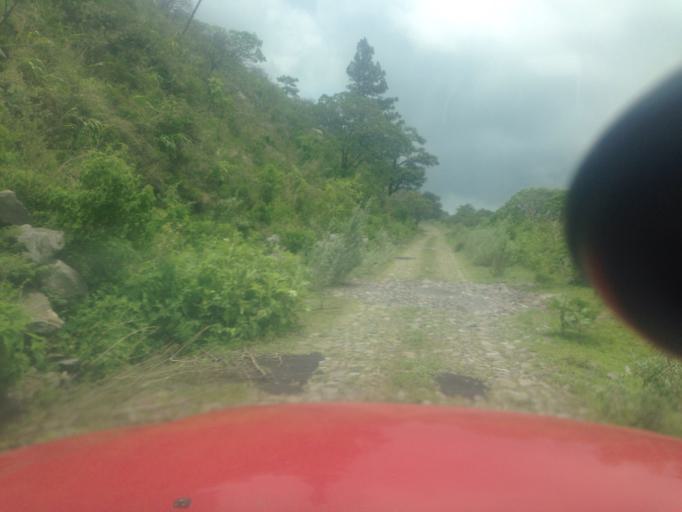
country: MX
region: Nayarit
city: Jala
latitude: 21.1227
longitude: -104.5000
